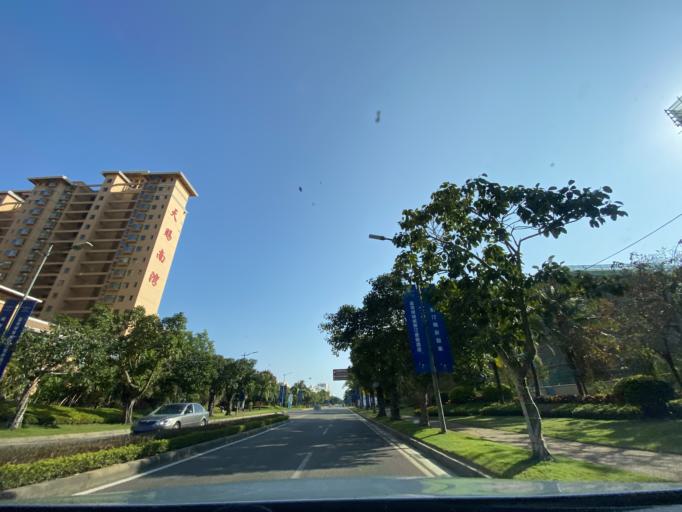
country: CN
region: Hainan
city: Xincun
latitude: 18.4217
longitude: 109.9610
